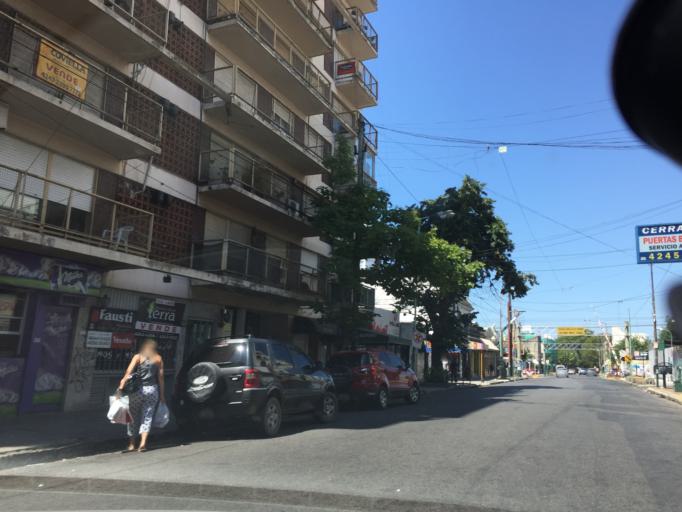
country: AR
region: Buenos Aires
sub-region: Partido de Lomas de Zamora
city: Lomas de Zamora
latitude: -34.7634
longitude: -58.3986
